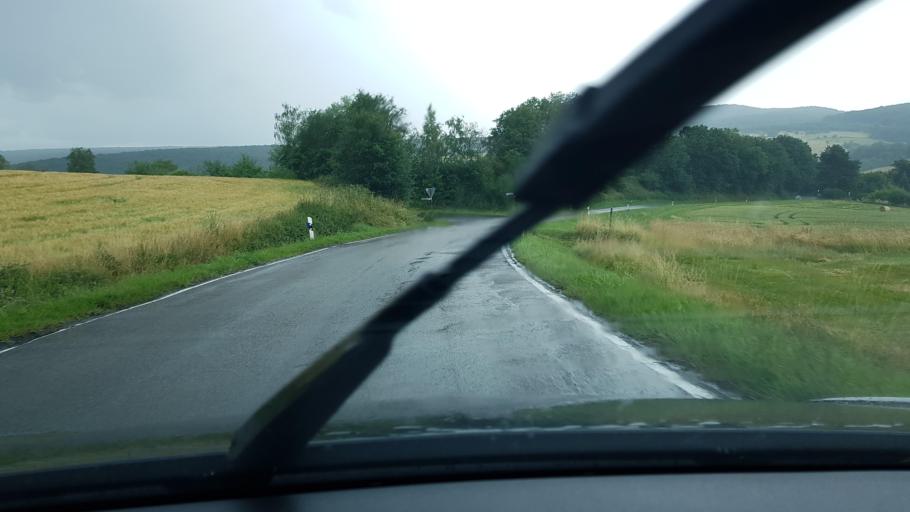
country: DE
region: Rheinland-Pfalz
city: Waldorf
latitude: 50.4915
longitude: 7.2304
